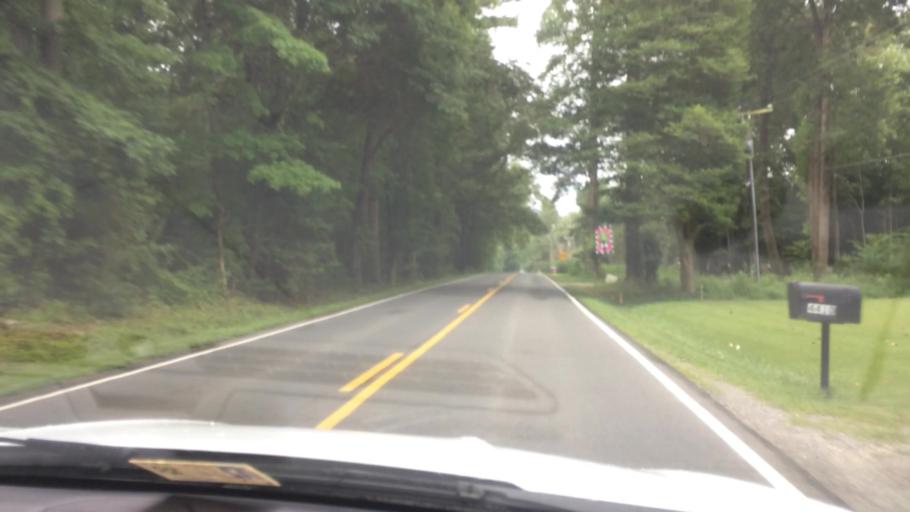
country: US
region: Virginia
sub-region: New Kent County
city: New Kent
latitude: 37.4588
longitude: -77.0357
